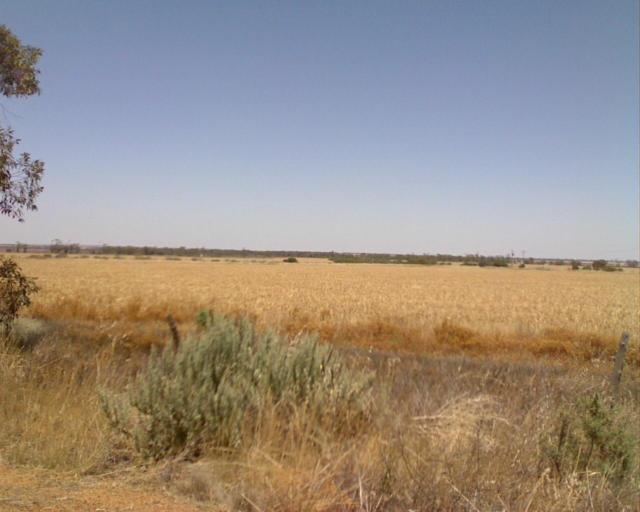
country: AU
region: Western Australia
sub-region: Wongan-Ballidu
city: Wongan Hills
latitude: -30.4524
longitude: 117.5256
